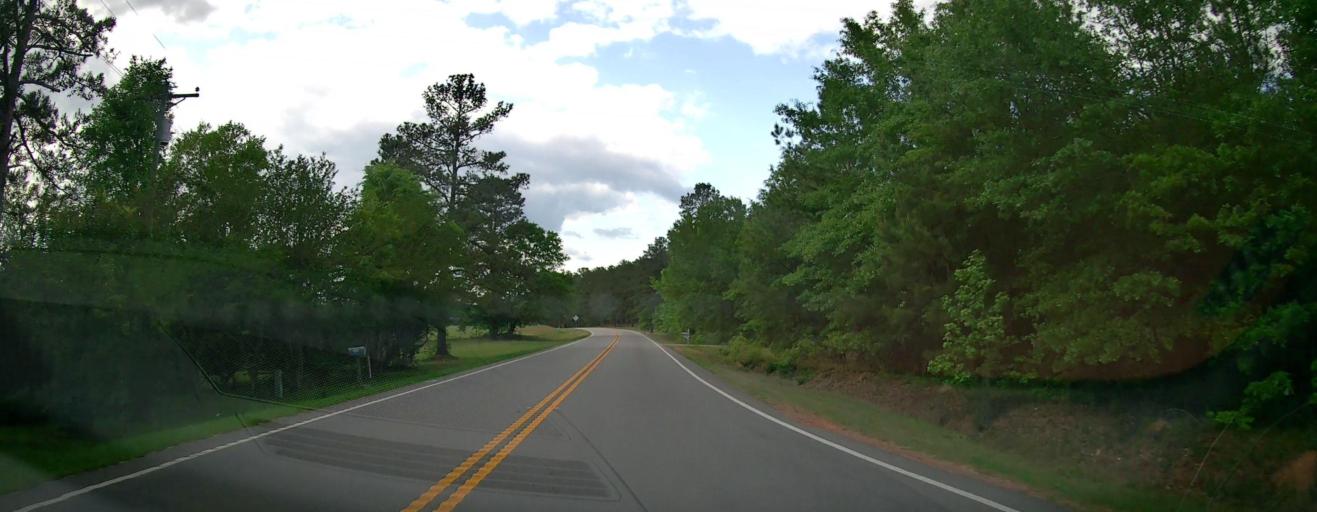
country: US
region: Georgia
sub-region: Baldwin County
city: Hardwick
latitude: 33.0536
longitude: -83.1239
